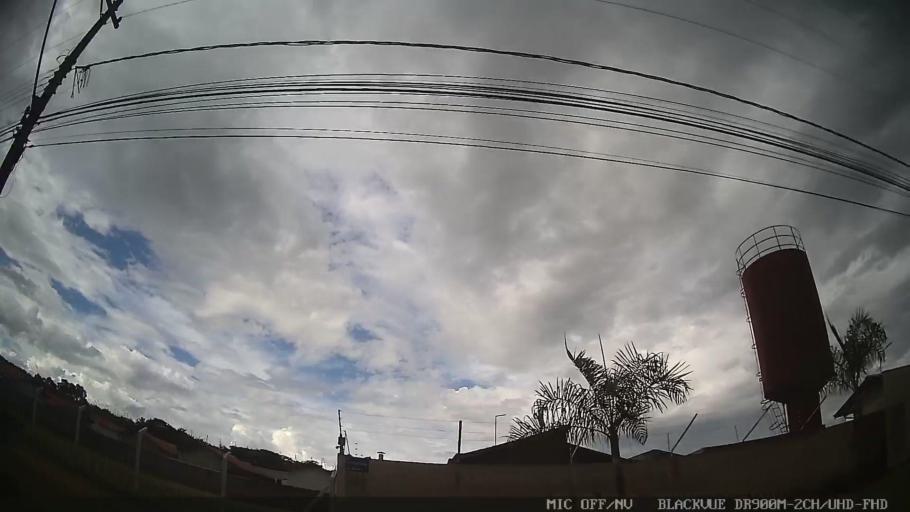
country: BR
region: Sao Paulo
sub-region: Jaguariuna
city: Jaguariuna
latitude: -22.6754
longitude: -46.9767
